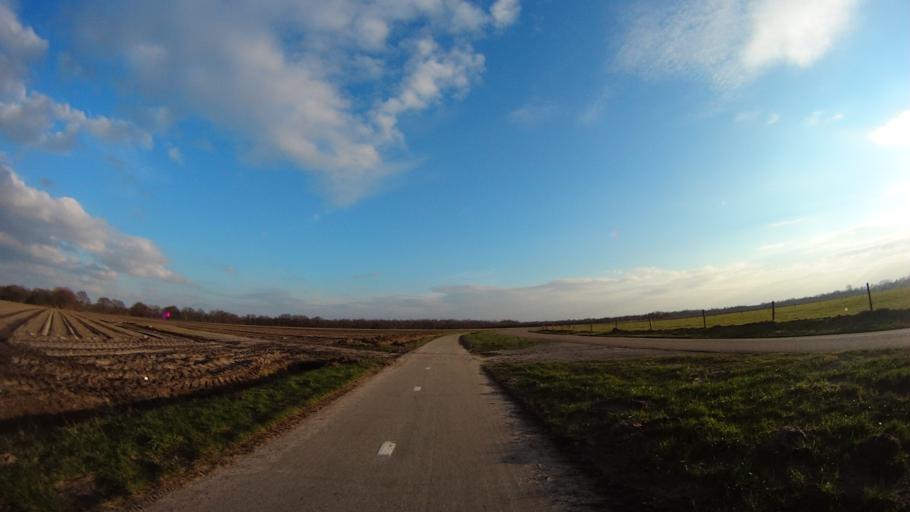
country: NL
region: Drenthe
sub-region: Gemeente Coevorden
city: Sleen
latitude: 52.8089
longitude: 6.7233
